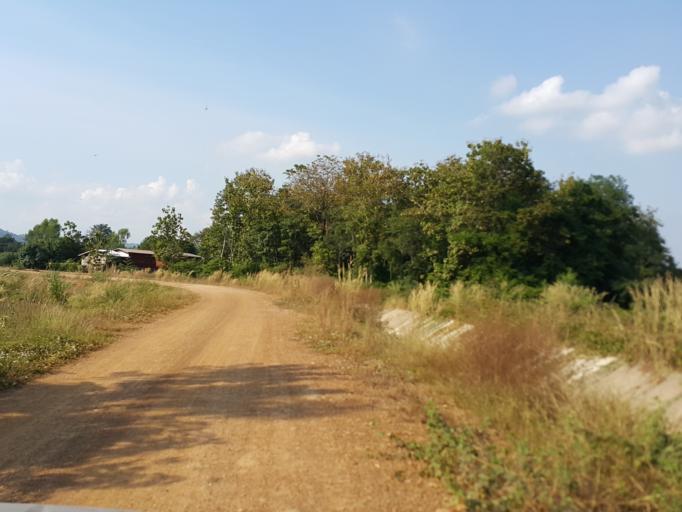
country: TH
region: Sukhothai
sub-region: Amphoe Si Satchanalai
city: Si Satchanalai
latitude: 17.4839
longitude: 99.6483
